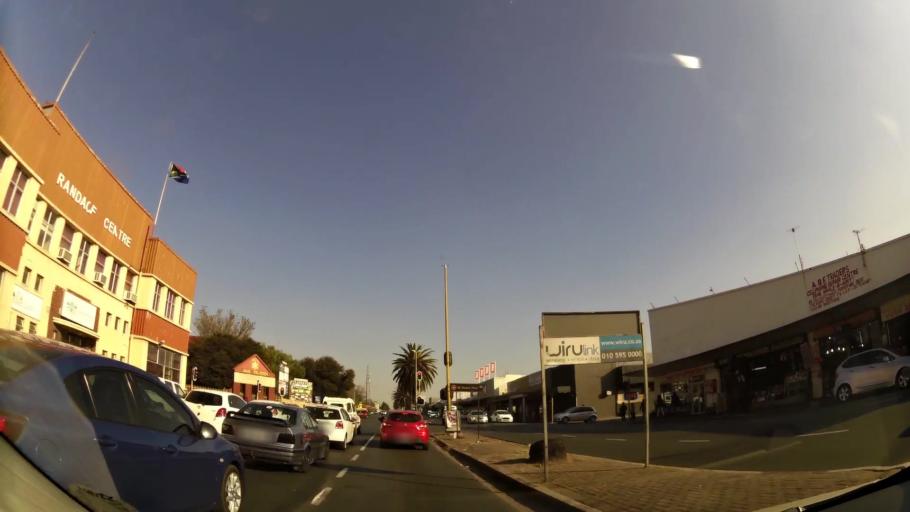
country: ZA
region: Gauteng
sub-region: West Rand District Municipality
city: Randfontein
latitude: -26.1820
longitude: 27.7039
